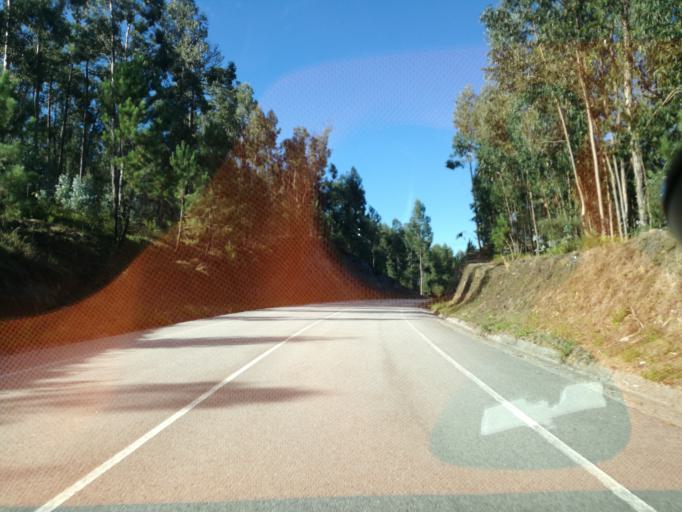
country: PT
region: Porto
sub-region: Pacos de Ferreira
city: Seroa
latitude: 41.2879
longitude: -8.4232
